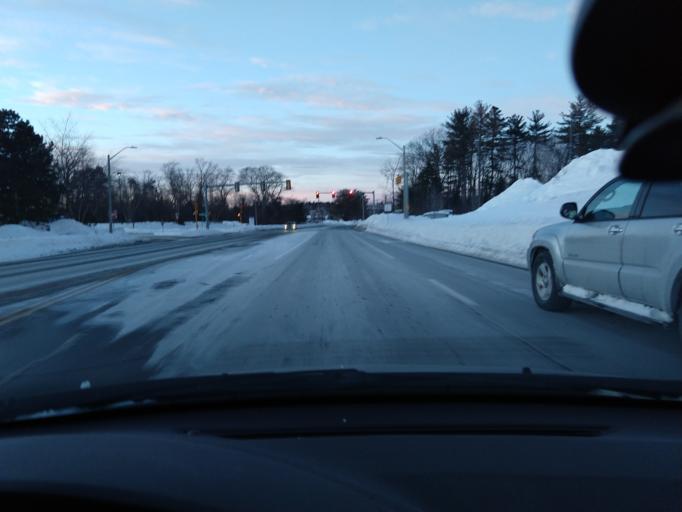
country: US
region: Massachusetts
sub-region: Middlesex County
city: Pinehurst
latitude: 42.4994
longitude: -71.2329
